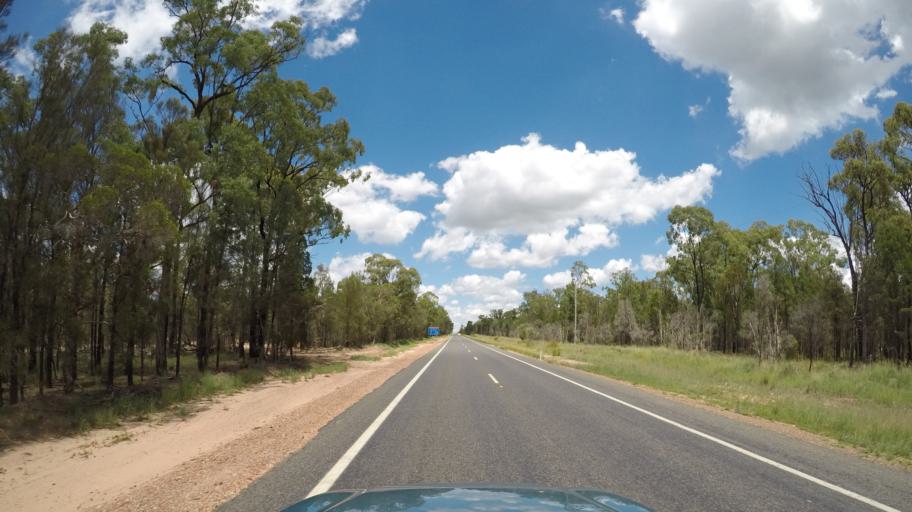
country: AU
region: Queensland
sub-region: Goondiwindi
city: Goondiwindi
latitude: -27.9956
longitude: 150.9492
